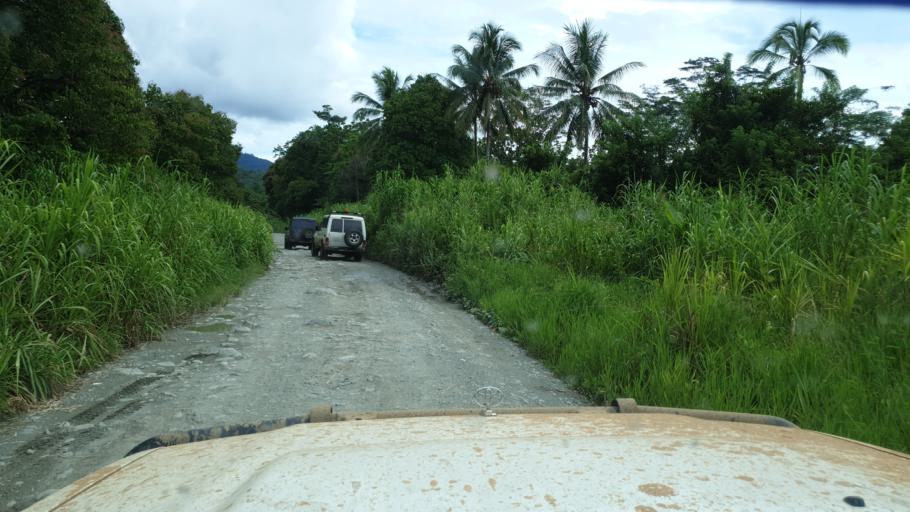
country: PG
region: Northern Province
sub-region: Sohe
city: Kokoda
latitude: -8.9188
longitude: 147.8656
